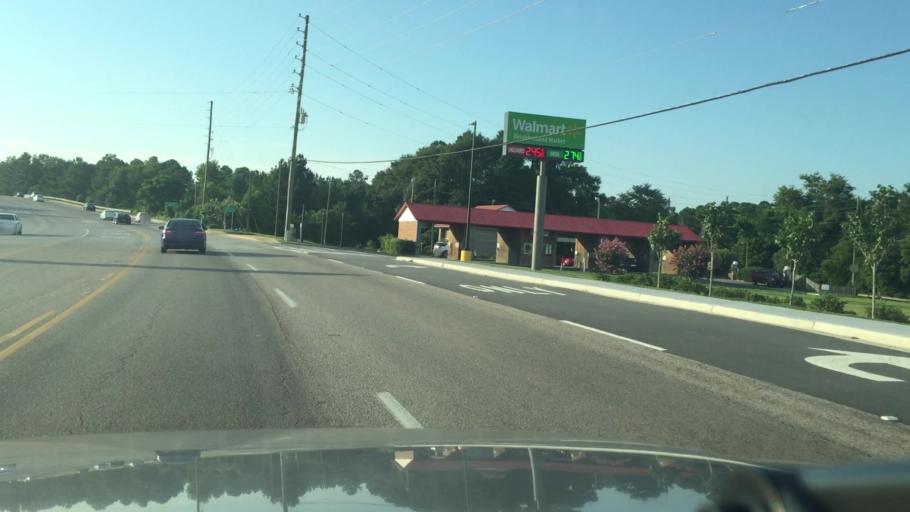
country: US
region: South Carolina
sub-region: Sumter County
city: South Sumter
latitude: 33.9060
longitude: -80.3794
